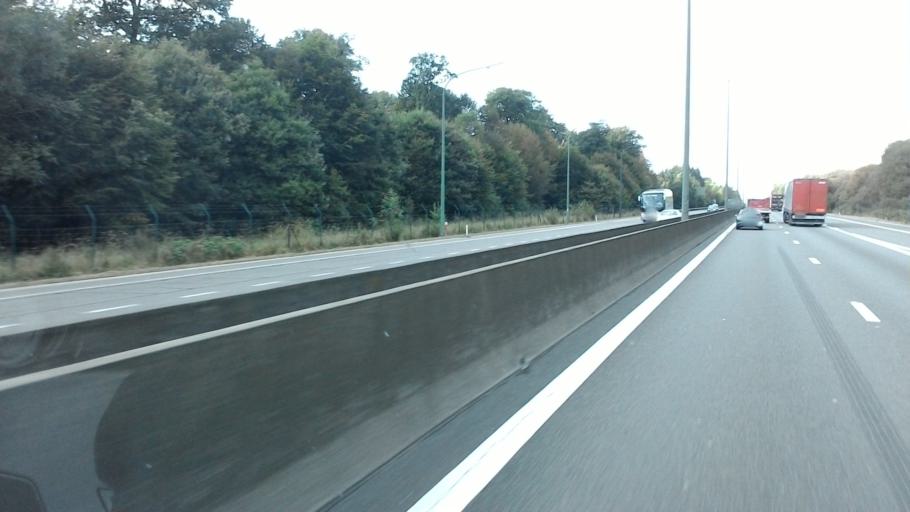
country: BE
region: Wallonia
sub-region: Province du Luxembourg
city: Habay-la-Vieille
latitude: 49.7502
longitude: 5.5681
